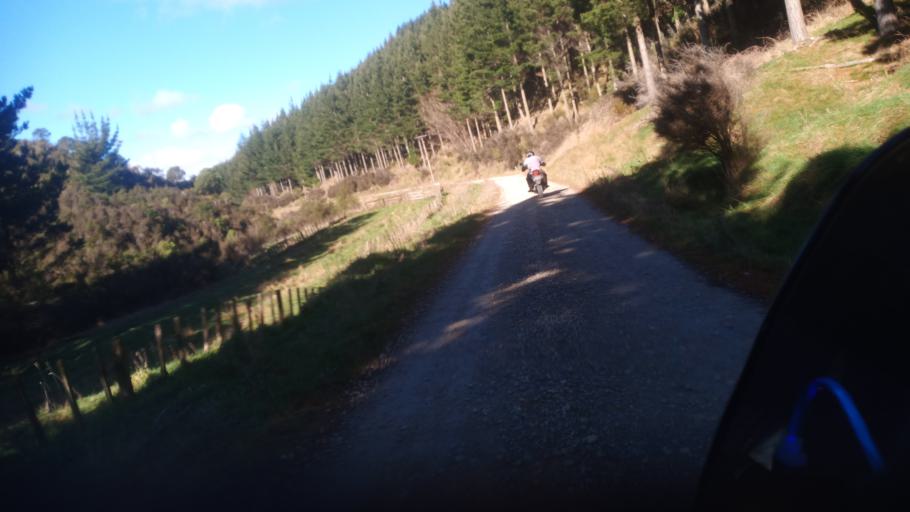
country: NZ
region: Hawke's Bay
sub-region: Wairoa District
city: Wairoa
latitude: -38.6570
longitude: 177.4931
